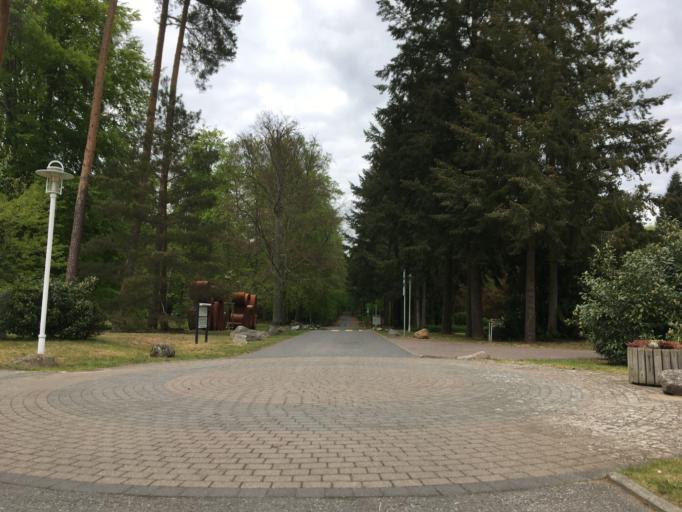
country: DE
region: Brandenburg
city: Wandlitz
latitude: 52.7323
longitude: 13.4898
